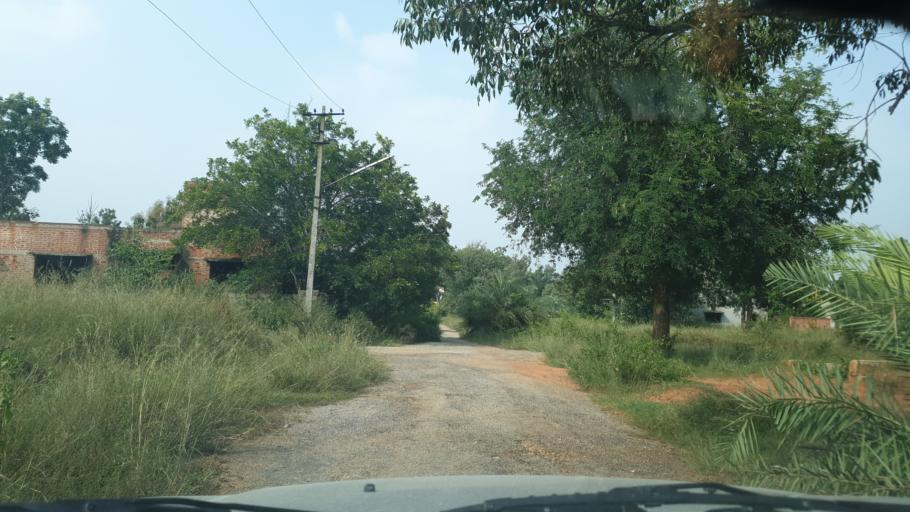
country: IN
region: Karnataka
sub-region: Bangalore Urban
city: Yelahanka
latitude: 13.0716
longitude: 77.6666
